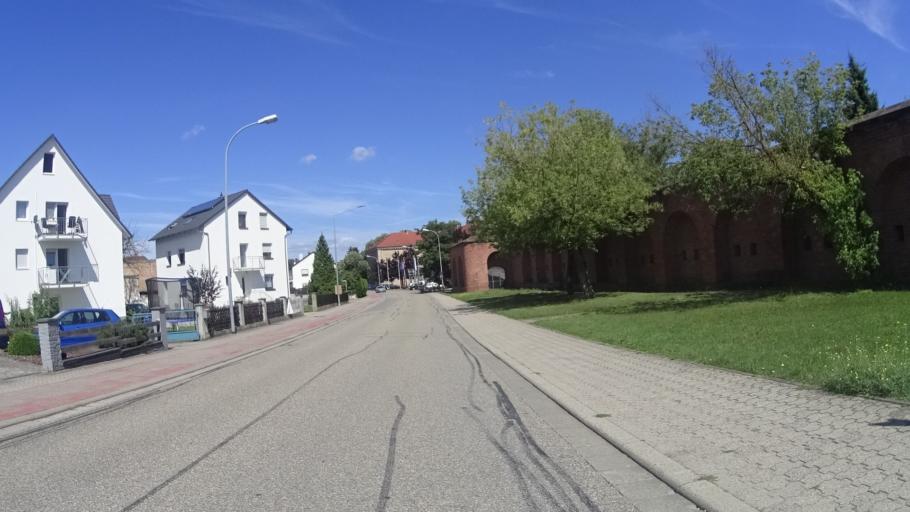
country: DE
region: Rheinland-Pfalz
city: Germersheim
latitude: 49.2203
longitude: 8.3762
